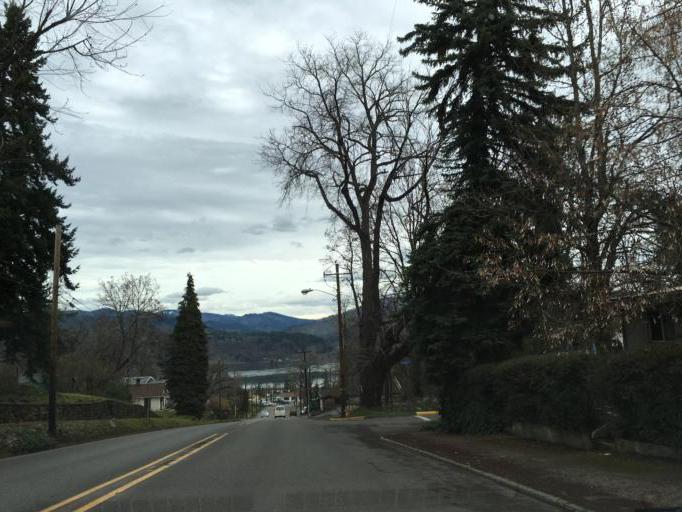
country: US
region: Oregon
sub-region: Hood River County
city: Hood River
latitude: 45.7062
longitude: -121.5252
